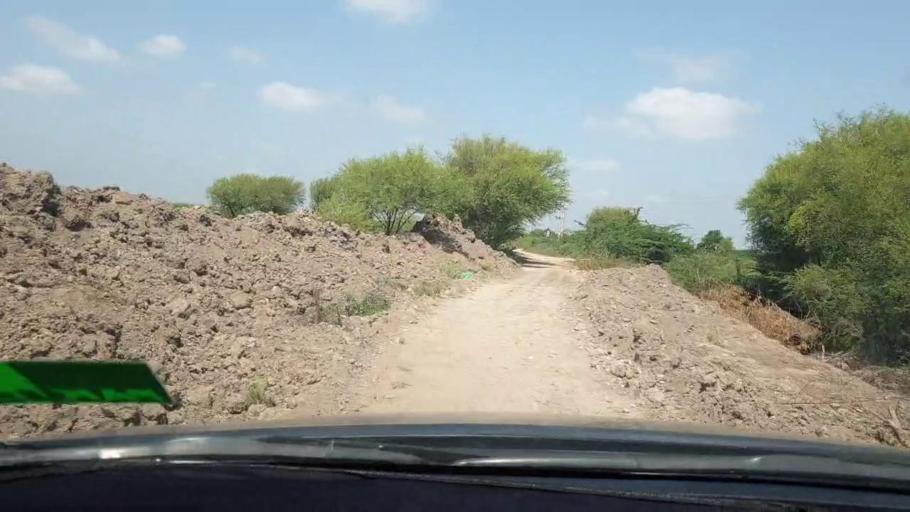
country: PK
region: Sindh
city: Tando Bago
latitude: 24.9459
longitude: 69.0983
